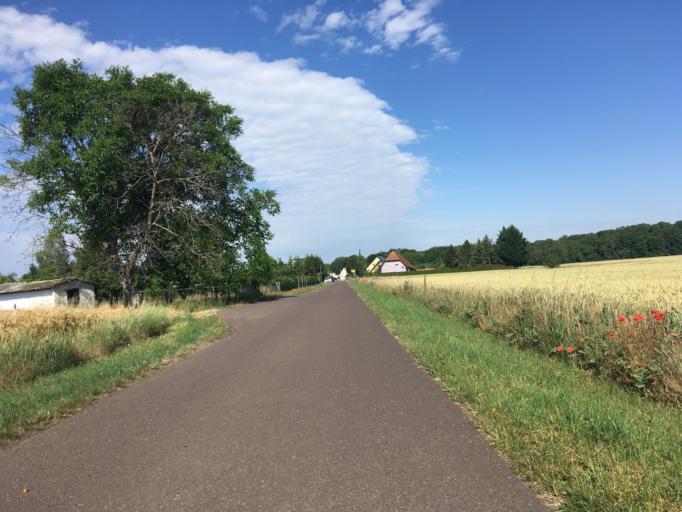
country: DE
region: Saxony-Anhalt
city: Wulfen
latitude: 51.7731
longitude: 11.9202
